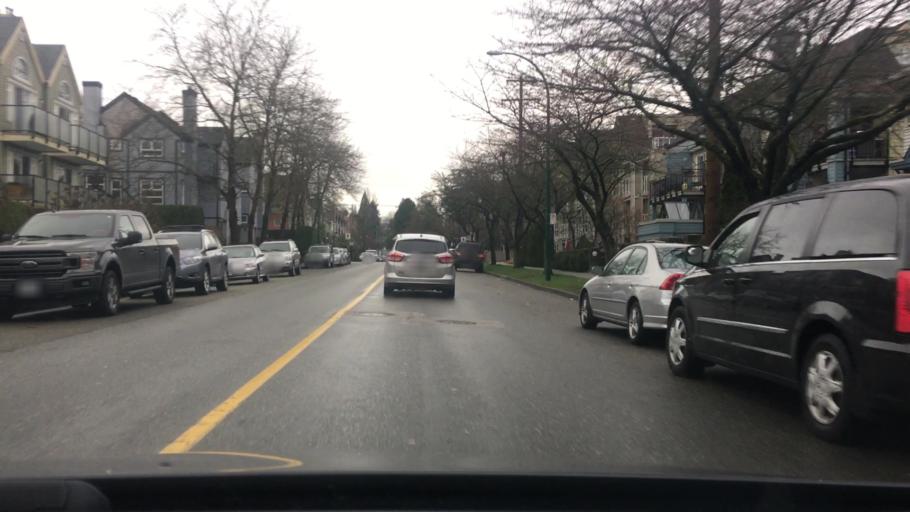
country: CA
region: British Columbia
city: Vancouver
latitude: 49.2570
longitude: -123.1230
